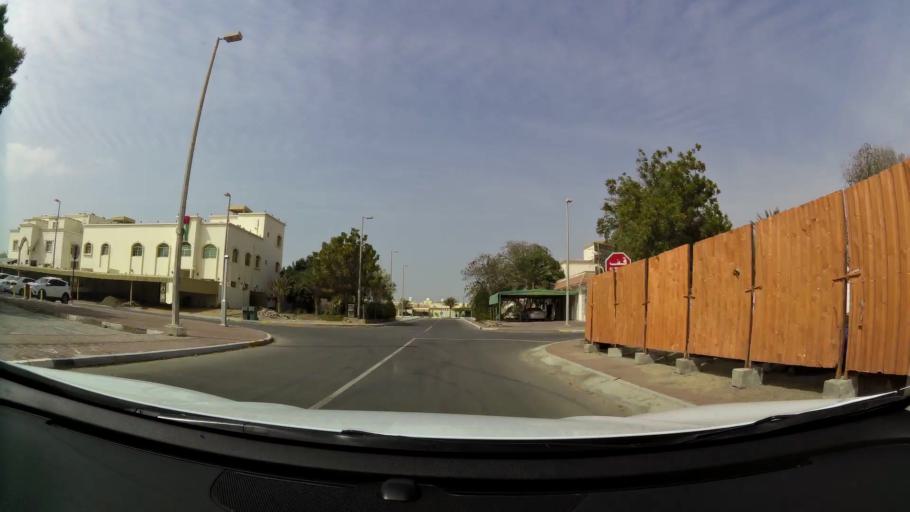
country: AE
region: Abu Dhabi
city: Abu Dhabi
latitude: 24.5531
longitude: 54.6819
